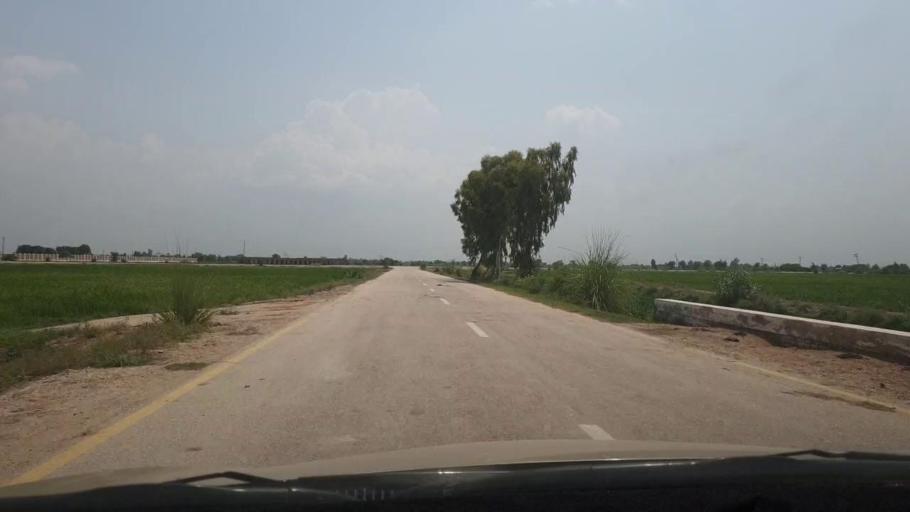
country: PK
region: Sindh
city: Naudero
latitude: 27.6970
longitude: 68.3337
